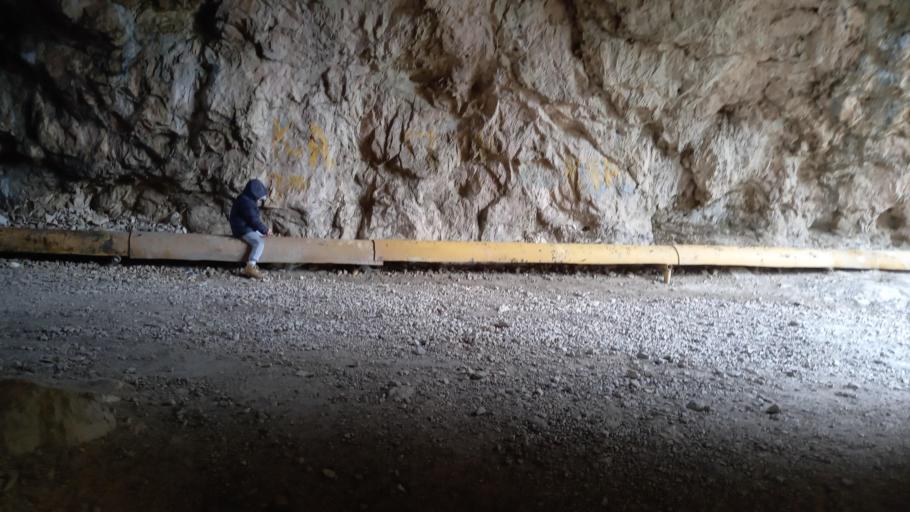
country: RU
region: Kabardino-Balkariya
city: Verkhnyaya Balkariya
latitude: 43.1876
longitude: 43.5150
